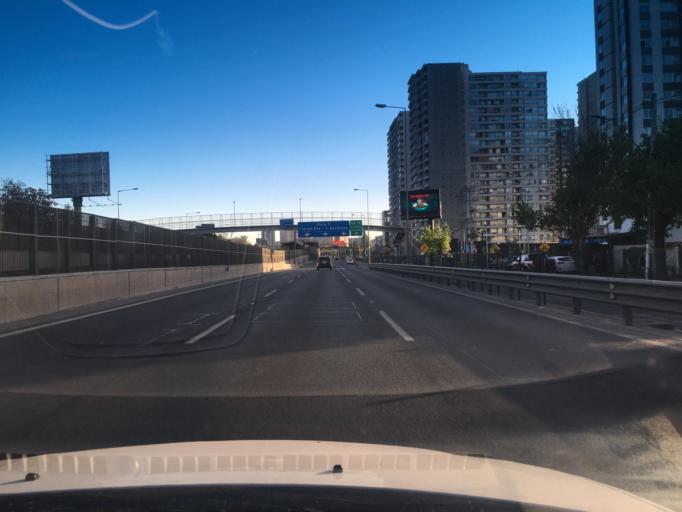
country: CL
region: Santiago Metropolitan
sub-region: Provincia de Santiago
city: Villa Presidente Frei, Nunoa, Santiago, Chile
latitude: -33.4962
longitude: -70.5848
